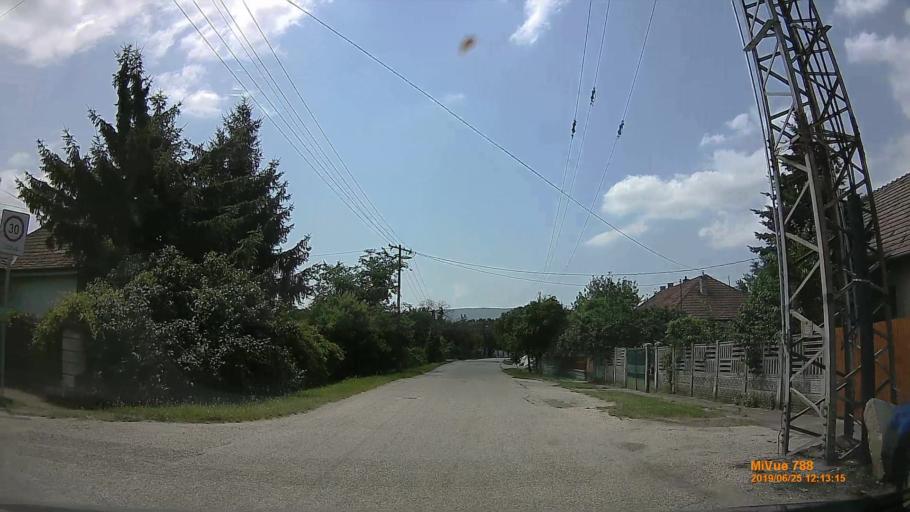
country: HU
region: Komarom-Esztergom
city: Dorog
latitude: 47.7415
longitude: 18.7176
